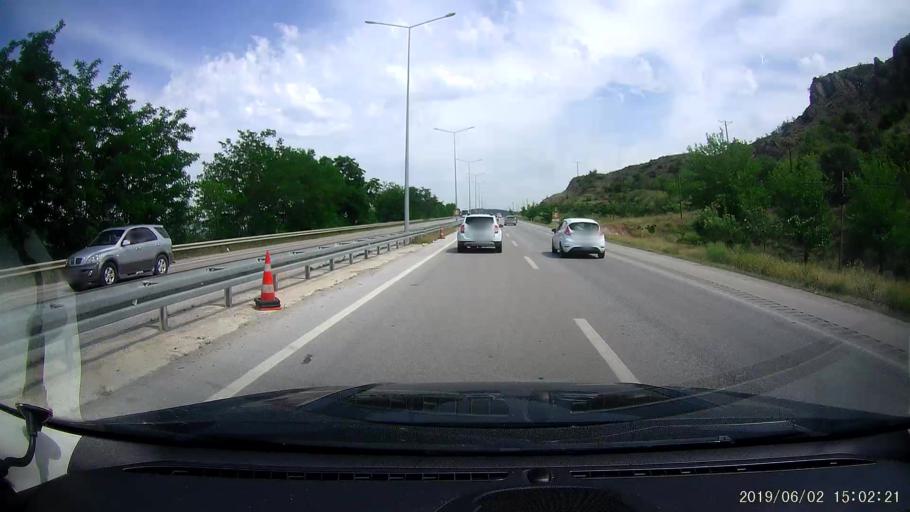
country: TR
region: Corum
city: Osmancik
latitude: 40.9818
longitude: 34.7658
